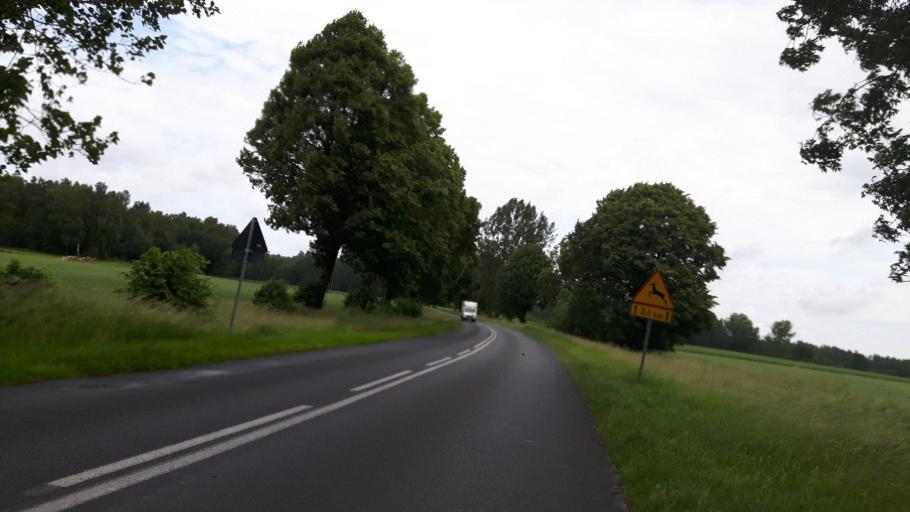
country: PL
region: West Pomeranian Voivodeship
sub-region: Powiat gryficki
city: Gryfice
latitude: 53.9831
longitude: 15.2395
